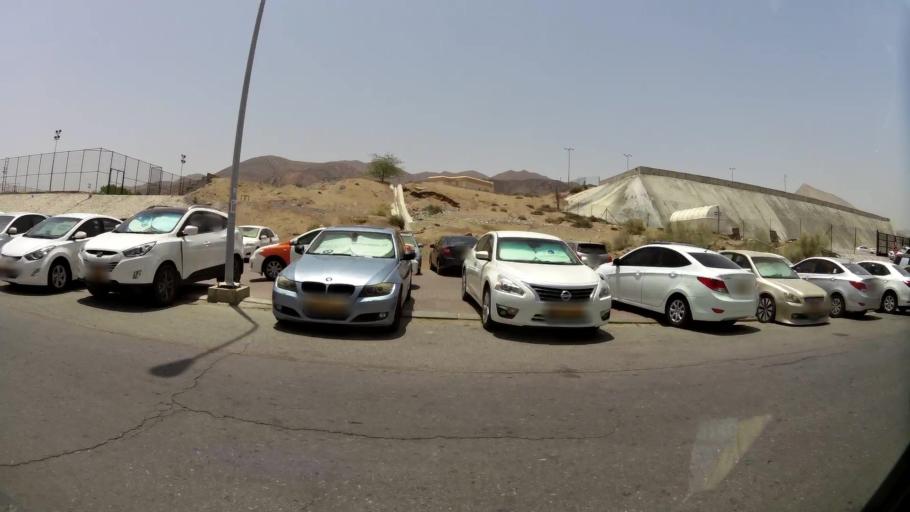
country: OM
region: Muhafazat Masqat
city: Bawshar
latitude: 23.5777
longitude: 58.4286
